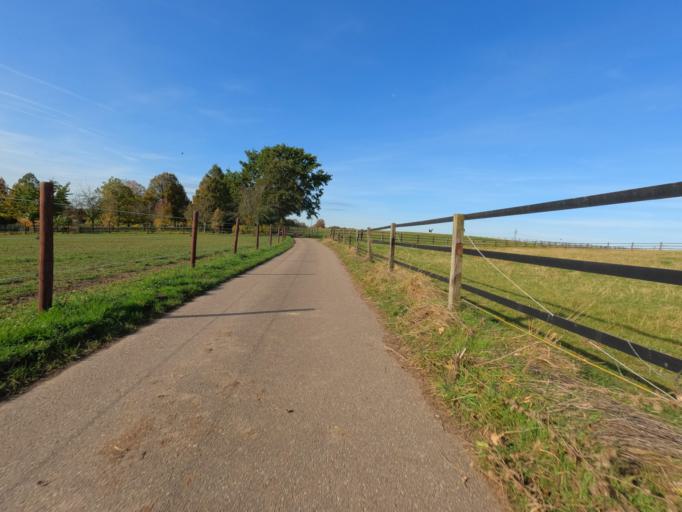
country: DE
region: North Rhine-Westphalia
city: Erkelenz
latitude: 51.0358
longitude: 6.3181
